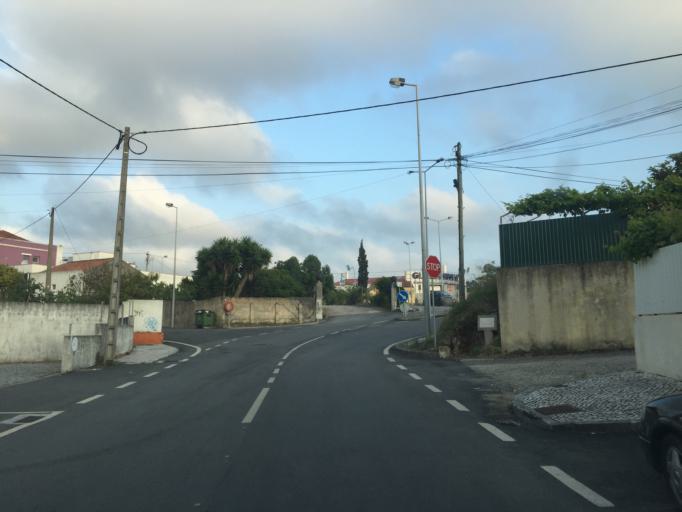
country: PT
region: Coimbra
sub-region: Figueira da Foz
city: Tavarede
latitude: 40.1651
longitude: -8.8385
